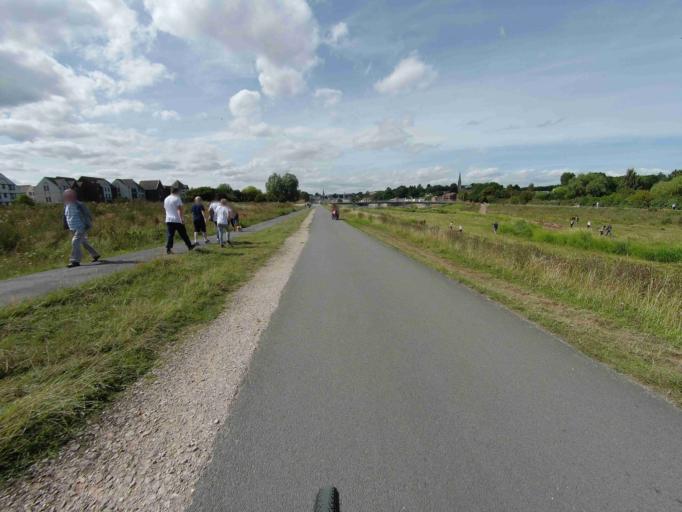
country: GB
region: England
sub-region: Devon
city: Exeter
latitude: 50.7116
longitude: -3.5243
